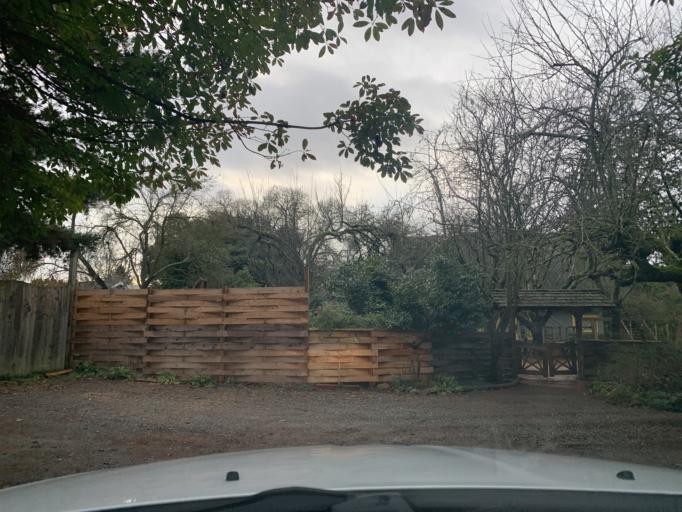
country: US
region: Washington
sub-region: King County
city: Seattle
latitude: 47.6648
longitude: -122.3392
